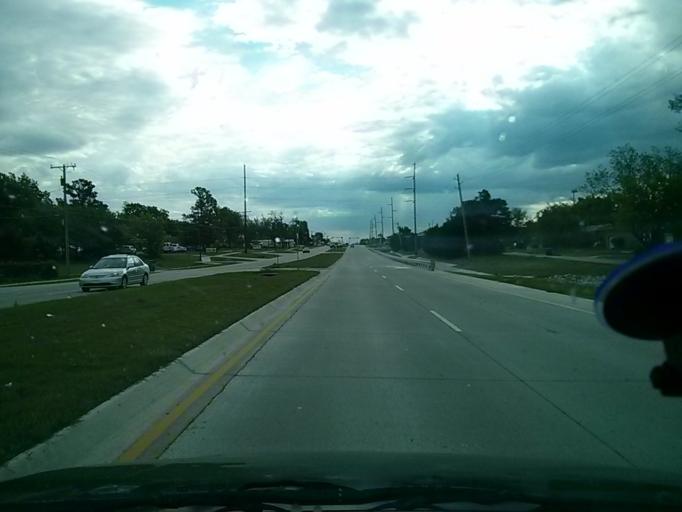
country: US
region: Oklahoma
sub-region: Tulsa County
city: Owasso
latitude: 36.1606
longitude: -95.8575
